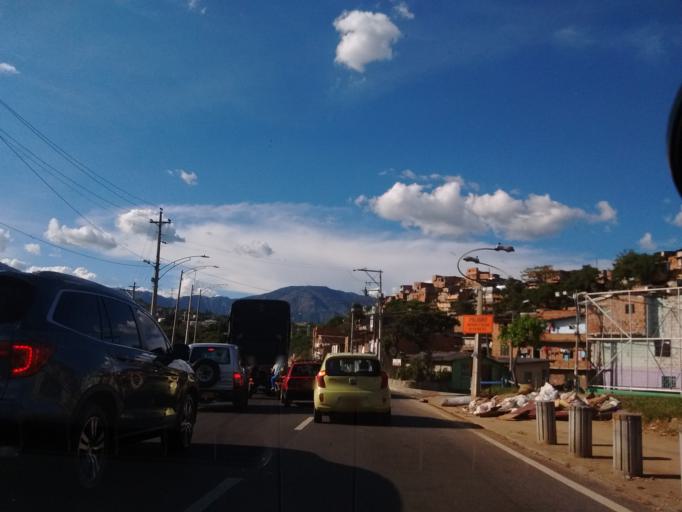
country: CO
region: Antioquia
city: Medellin
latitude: 6.2808
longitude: -75.5681
